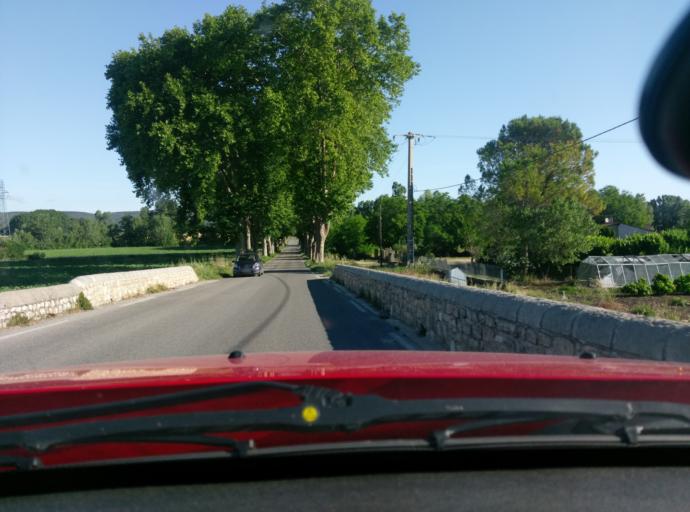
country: FR
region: Languedoc-Roussillon
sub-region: Departement du Gard
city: Uzes
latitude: 44.0310
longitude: 4.4111
